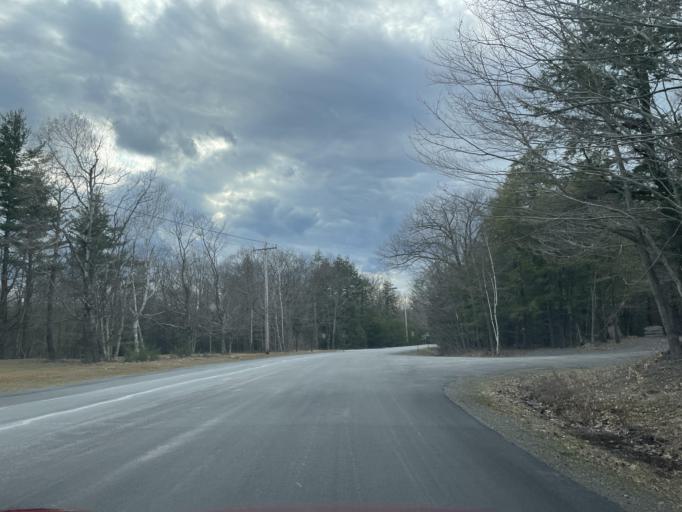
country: US
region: New York
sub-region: Greene County
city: Palenville
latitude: 42.2015
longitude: -74.0567
